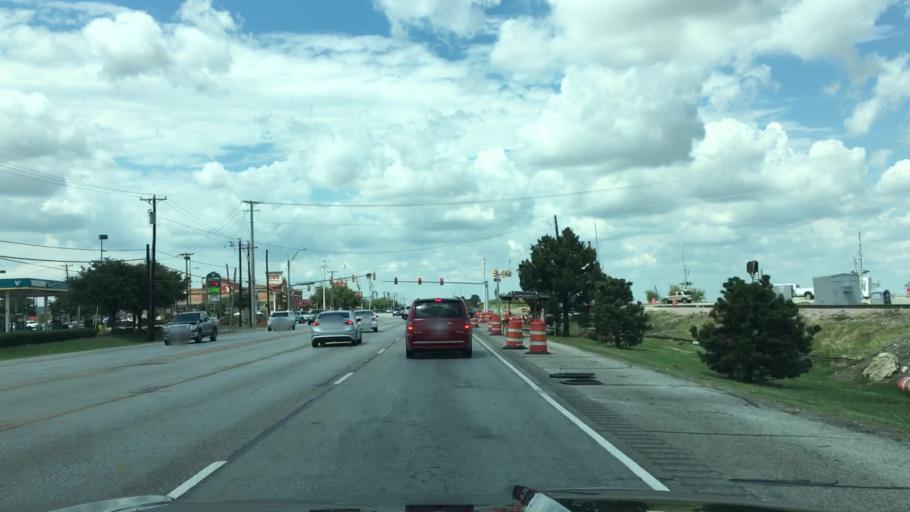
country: US
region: Texas
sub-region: Tarrant County
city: Saginaw
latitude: 32.8799
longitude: -97.3808
